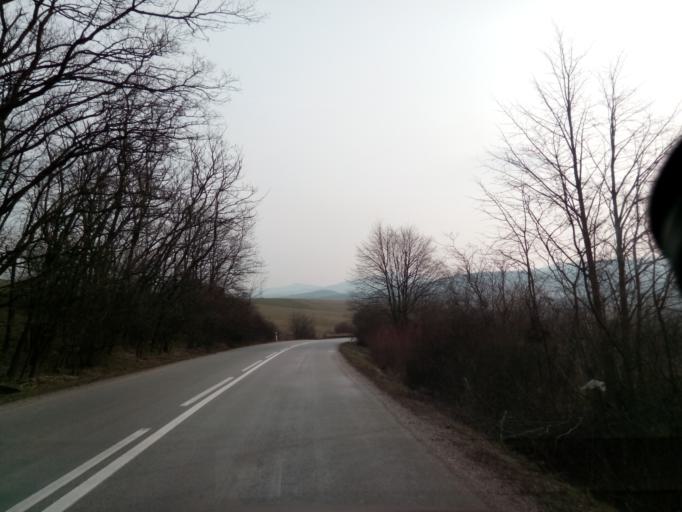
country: SK
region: Kosicky
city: Secovce
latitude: 48.6283
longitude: 21.5540
